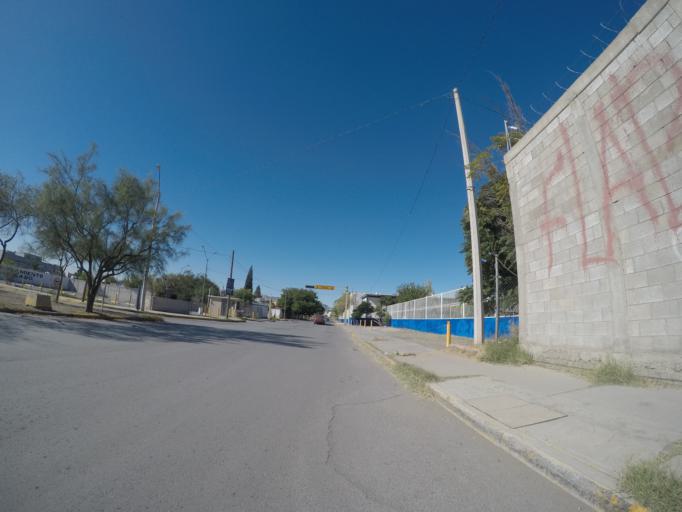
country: MX
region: Chihuahua
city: Ciudad Juarez
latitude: 31.7440
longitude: -106.4471
